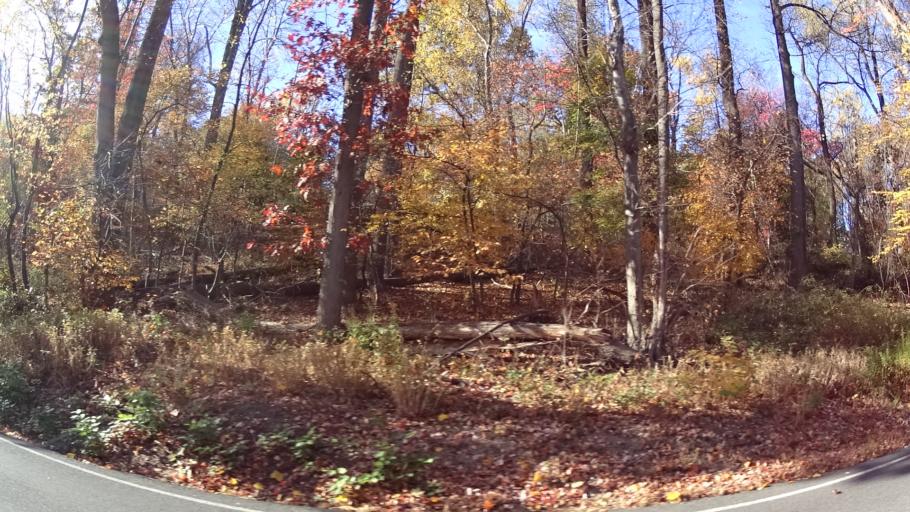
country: US
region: New Jersey
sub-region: Union County
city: Mountainside
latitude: 40.6799
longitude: -74.3664
